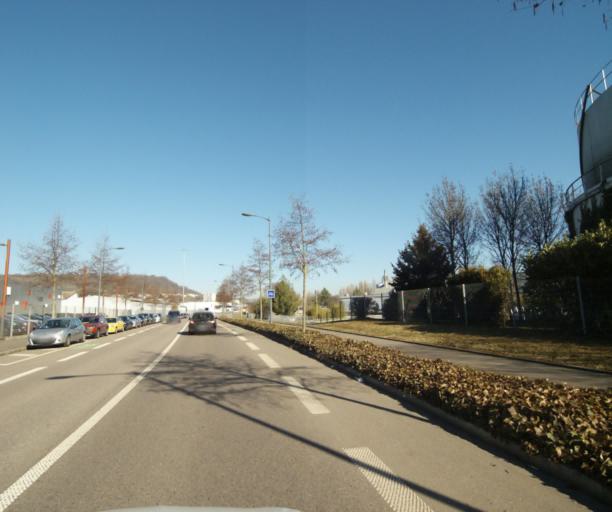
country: FR
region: Lorraine
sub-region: Departement de Meurthe-et-Moselle
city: Maxeville
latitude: 48.7114
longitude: 6.1726
